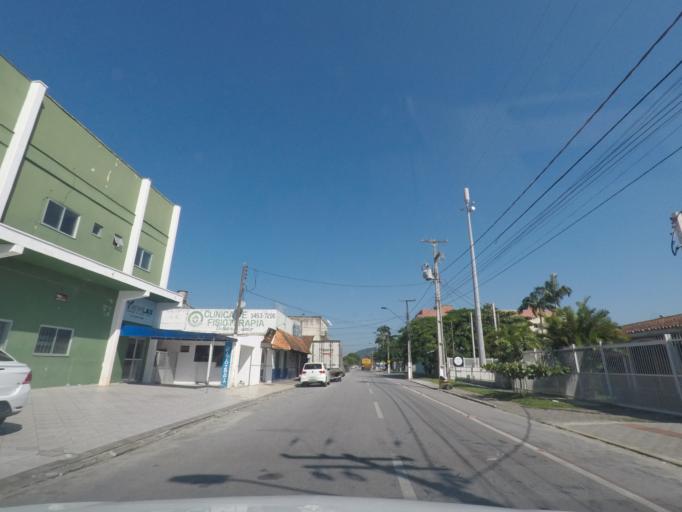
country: BR
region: Parana
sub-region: Guaratuba
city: Guaratuba
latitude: -25.8201
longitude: -48.5342
